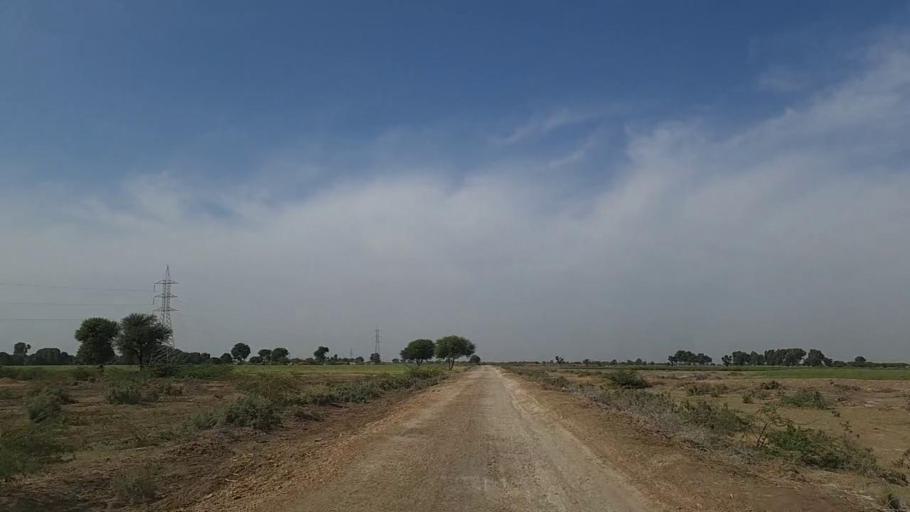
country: PK
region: Sindh
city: Samaro
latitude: 25.2151
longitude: 69.4532
